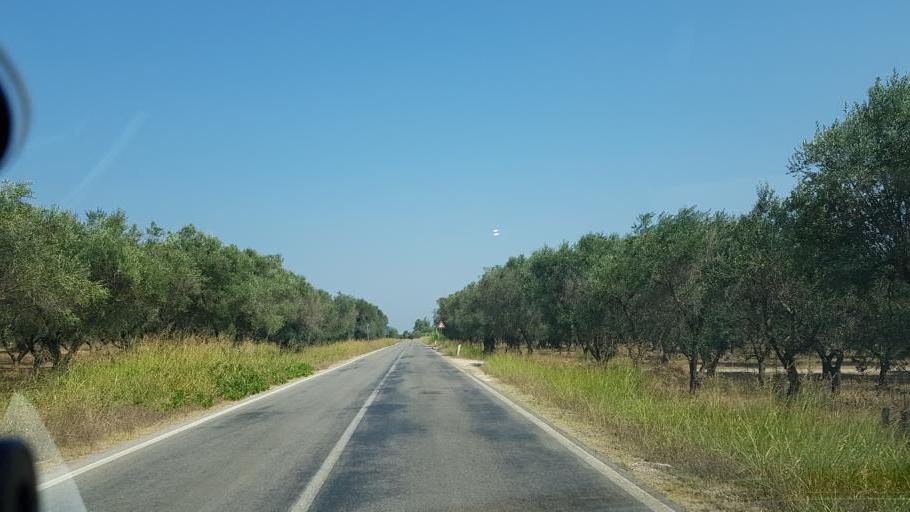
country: IT
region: Apulia
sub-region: Provincia di Brindisi
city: Torre Santa Susanna
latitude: 40.4976
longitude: 17.7441
